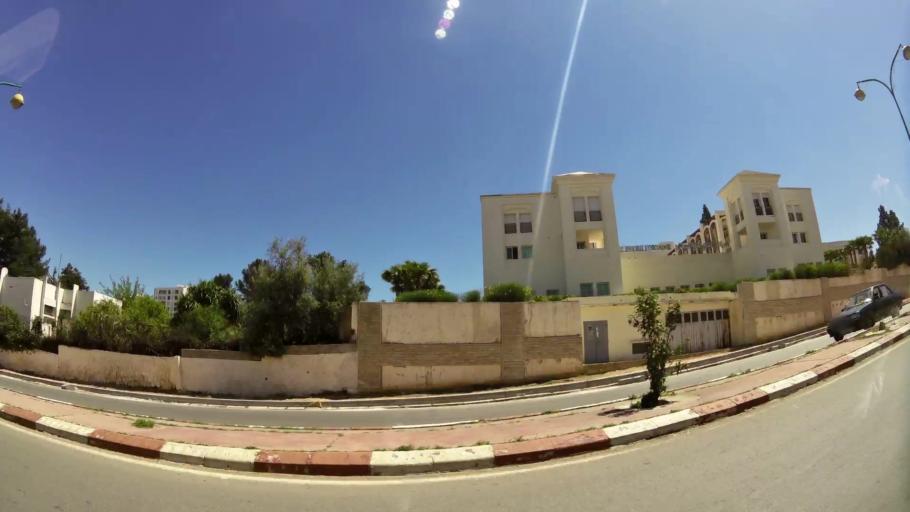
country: MA
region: Meknes-Tafilalet
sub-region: Meknes
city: Meknes
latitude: 33.8930
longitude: -5.5483
